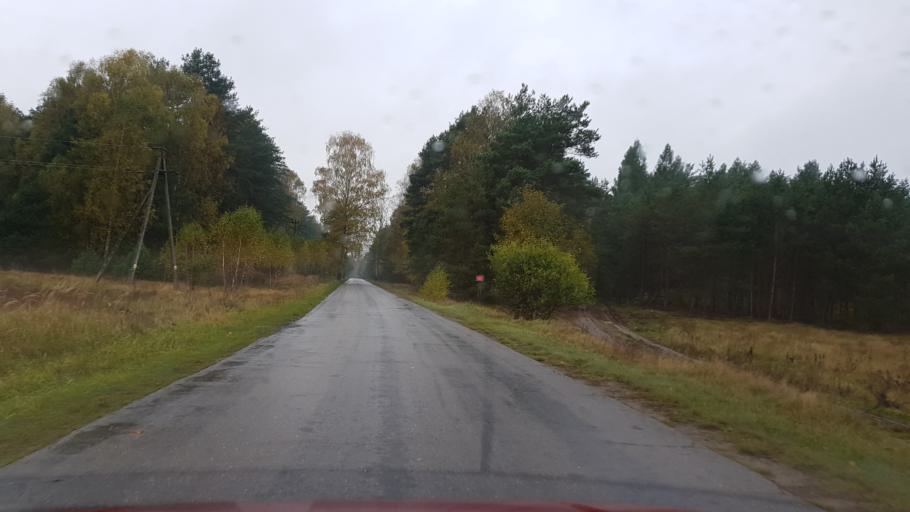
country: PL
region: West Pomeranian Voivodeship
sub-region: Powiat walecki
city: Walcz
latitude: 53.3536
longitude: 16.5563
